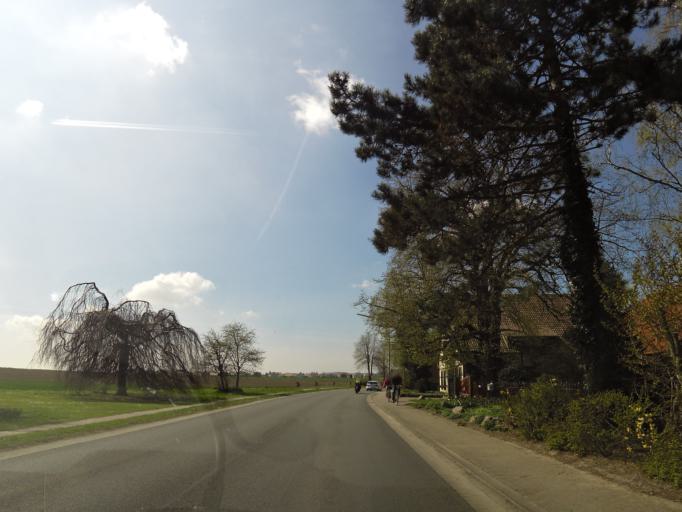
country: DE
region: Lower Saxony
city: Hagenburg
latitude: 52.4370
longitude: 9.3408
